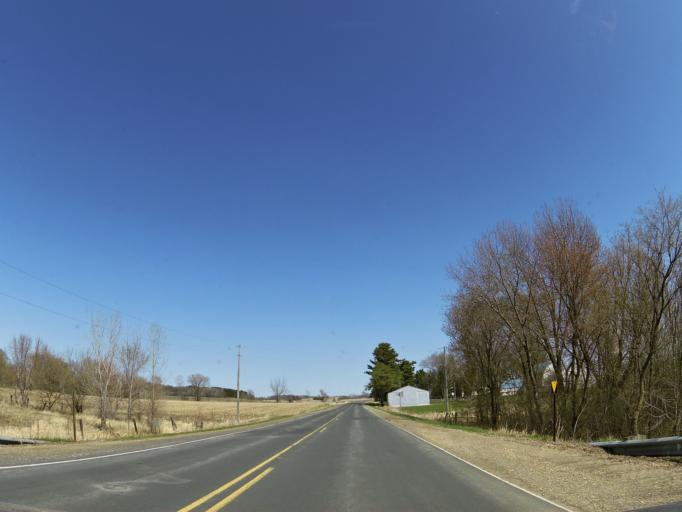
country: US
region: Wisconsin
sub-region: Saint Croix County
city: Roberts
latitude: 44.9350
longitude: -92.5288
